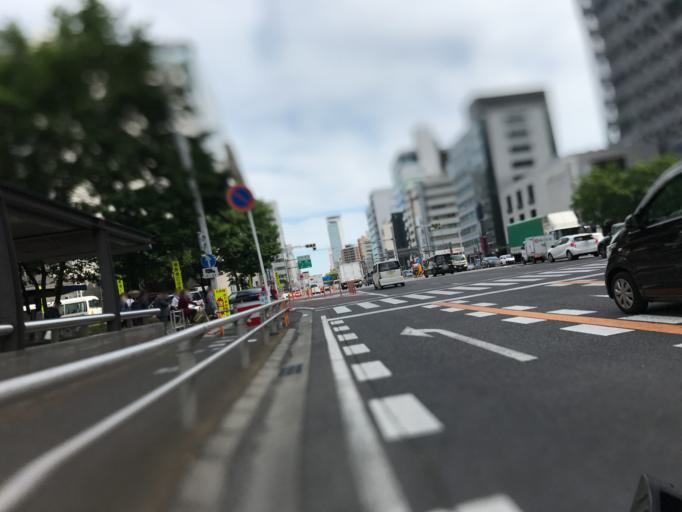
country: JP
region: Aichi
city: Nagoya-shi
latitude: 35.1675
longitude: 136.8977
